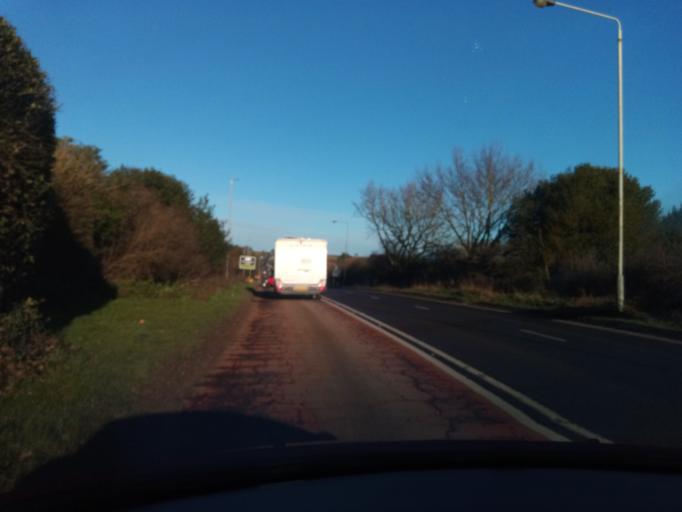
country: GB
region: England
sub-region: Nottinghamshire
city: Farnsfield
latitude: 53.1056
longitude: -1.0635
